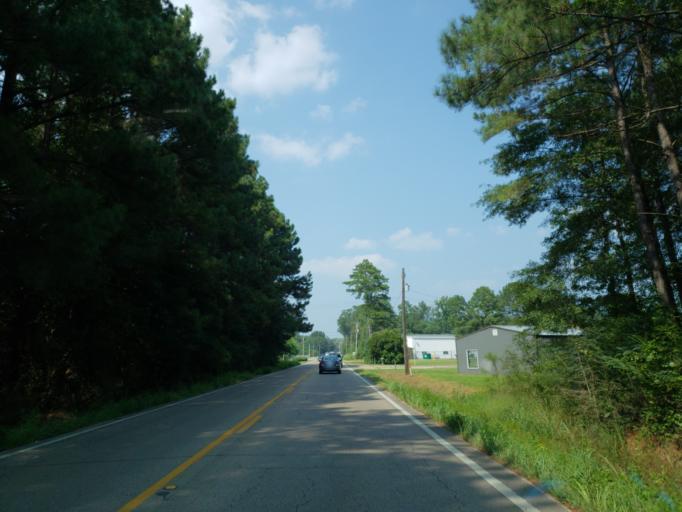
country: US
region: Mississippi
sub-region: Jones County
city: Ellisville
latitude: 31.6399
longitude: -89.1798
